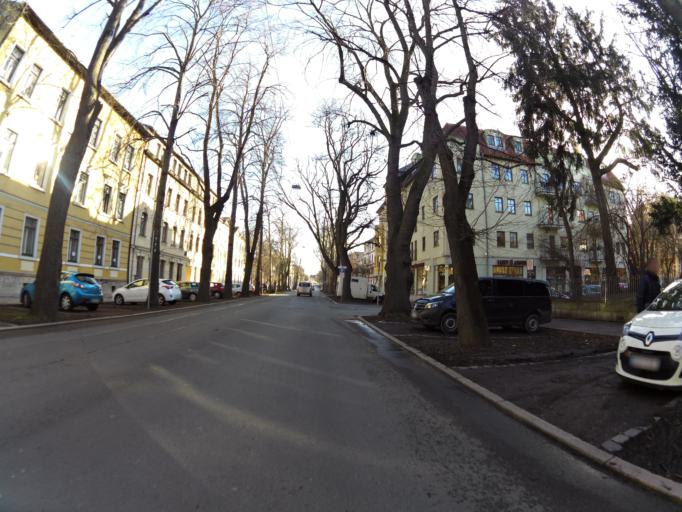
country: DE
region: Thuringia
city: Weimar
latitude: 50.9785
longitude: 11.3213
